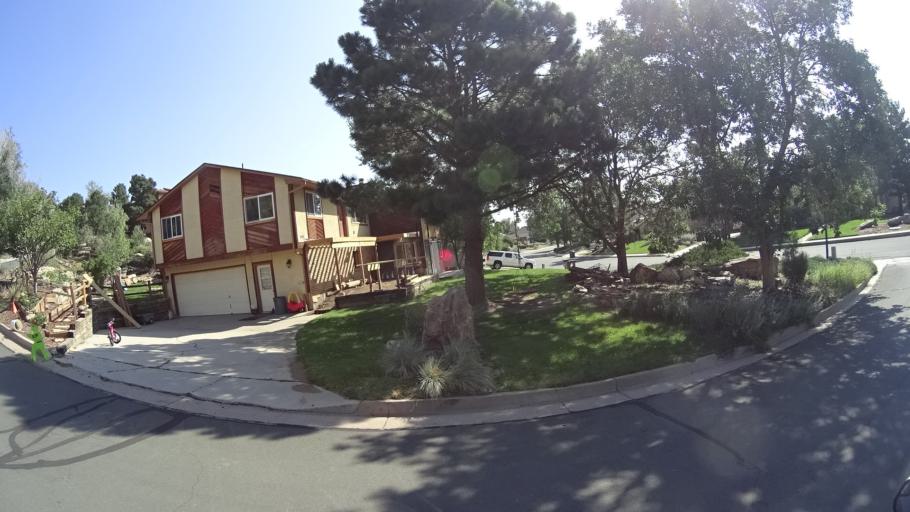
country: US
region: Colorado
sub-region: El Paso County
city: Manitou Springs
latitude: 38.9069
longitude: -104.8756
